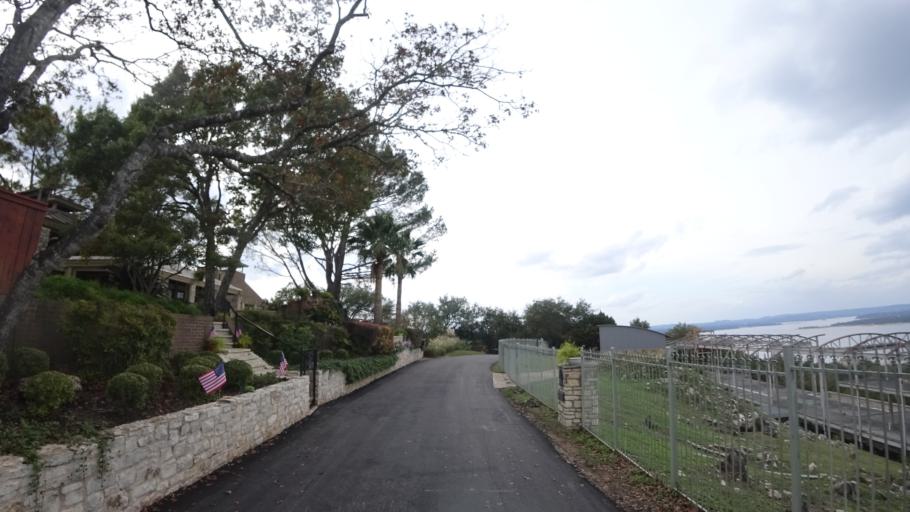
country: US
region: Texas
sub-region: Travis County
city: Hudson Bend
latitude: 30.3918
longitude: -97.8821
